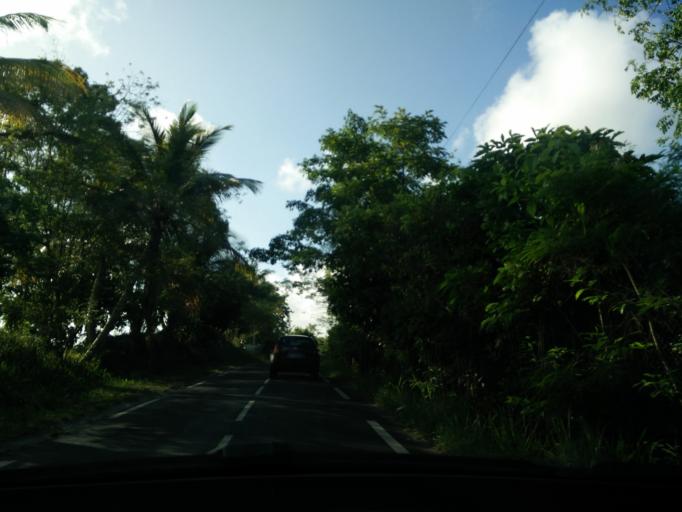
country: GP
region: Guadeloupe
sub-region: Guadeloupe
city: Sainte-Anne
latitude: 16.2740
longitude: -61.4233
